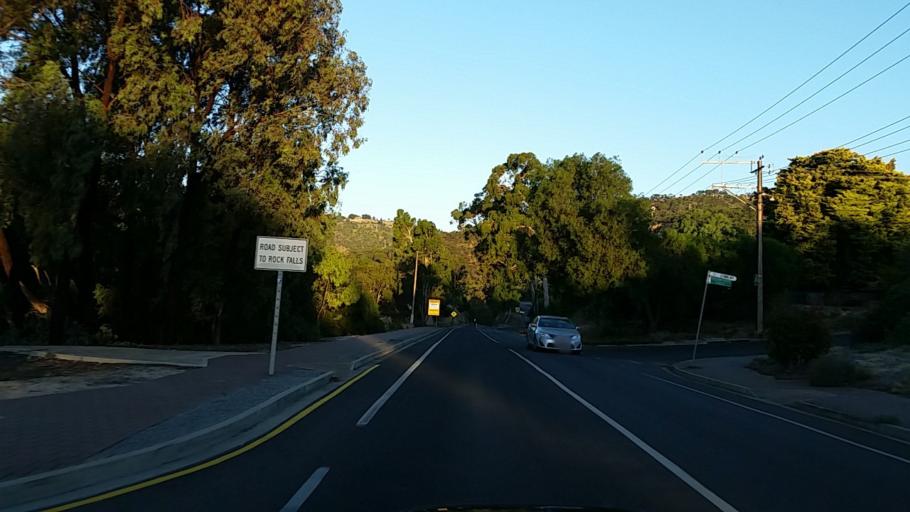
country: AU
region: South Australia
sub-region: Campbelltown
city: Athelstone
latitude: -34.8642
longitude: 138.7131
